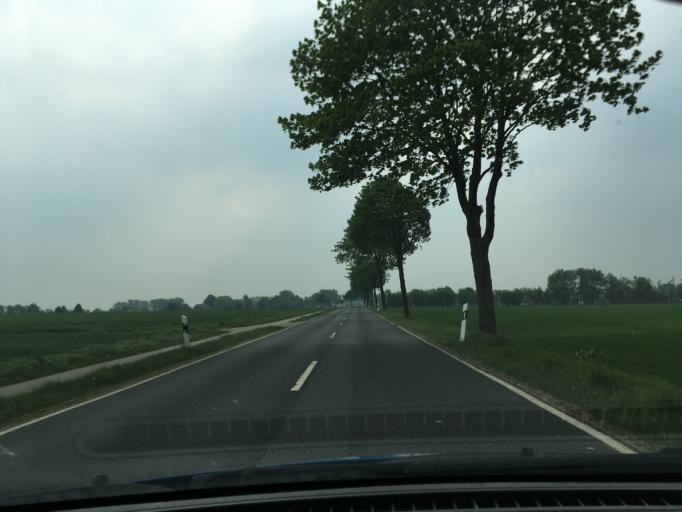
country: DE
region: Lower Saxony
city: Buchholz in der Nordheide
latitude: 53.3899
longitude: 9.8600
